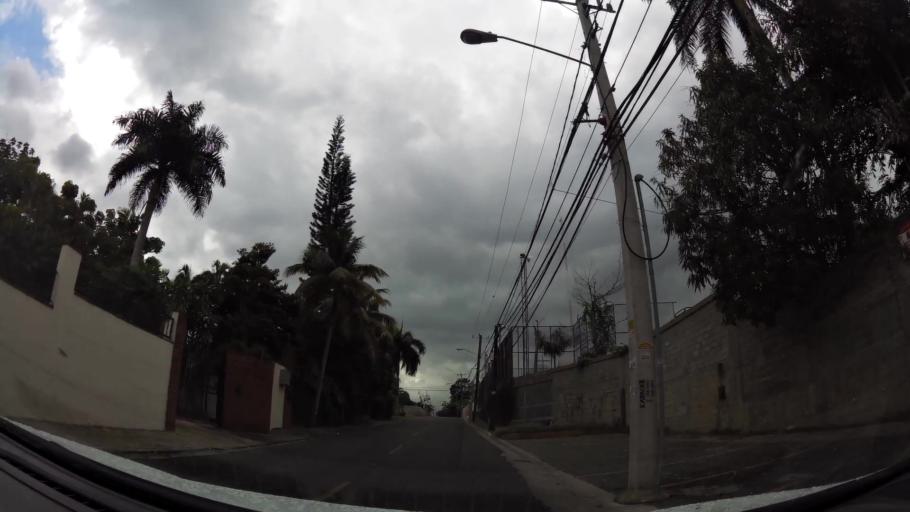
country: DO
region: Nacional
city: La Agustina
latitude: 18.4973
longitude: -69.9376
